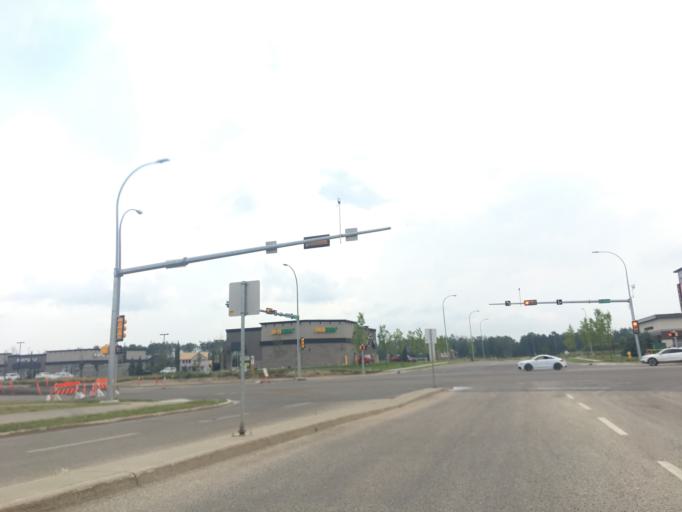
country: CA
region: Alberta
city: Grande Prairie
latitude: 55.1422
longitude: -118.8079
